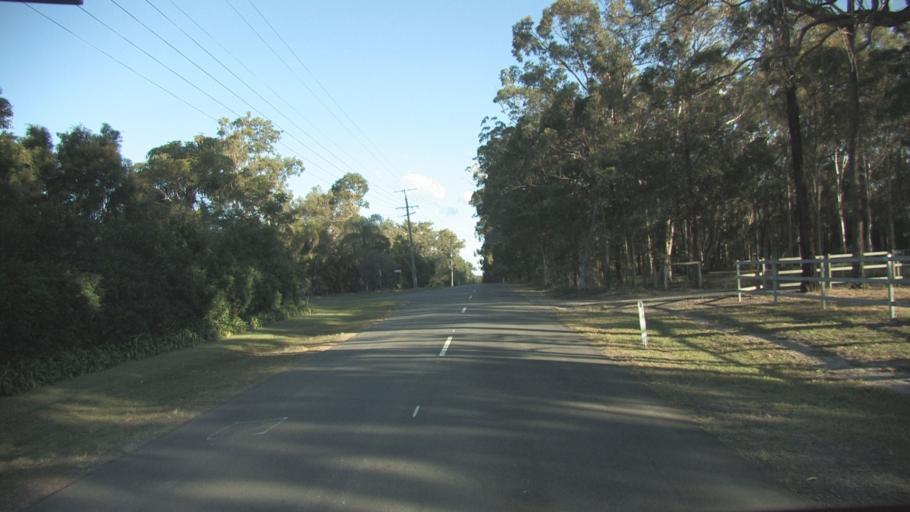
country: AU
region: Queensland
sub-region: Gold Coast
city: Yatala
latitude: -27.6784
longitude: 153.2755
